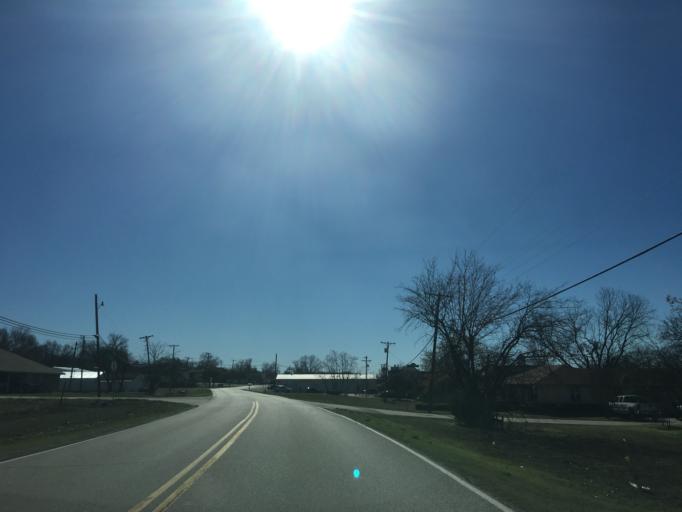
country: US
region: Texas
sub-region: Collin County
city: Prosper
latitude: 33.2386
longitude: -96.8023
